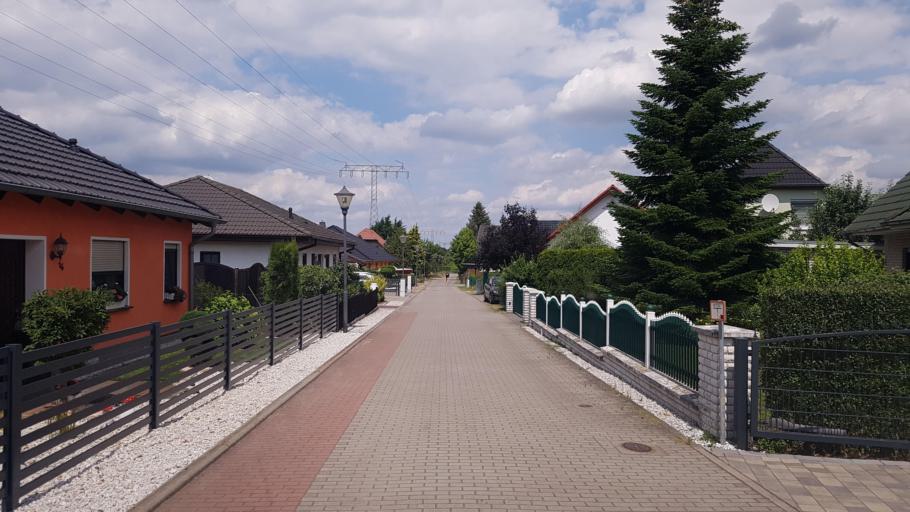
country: DE
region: Brandenburg
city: Brandenburg an der Havel
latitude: 52.3632
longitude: 12.5563
